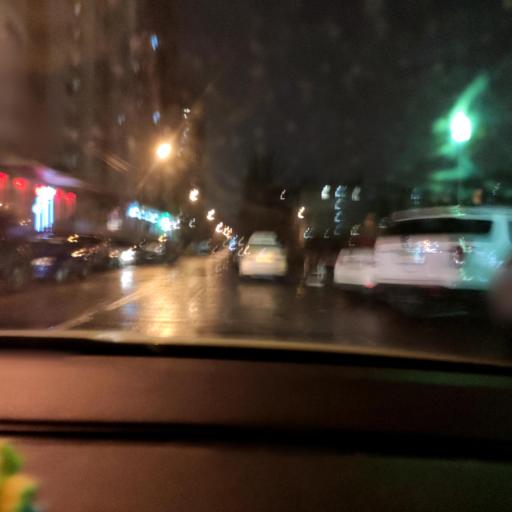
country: RU
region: Moskovskaya
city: Reutov
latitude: 55.7567
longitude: 37.8508
